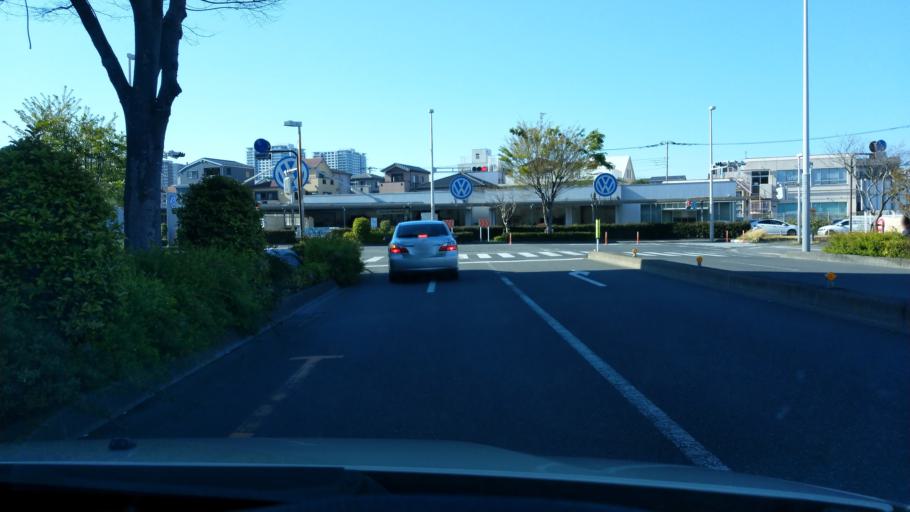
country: JP
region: Saitama
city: Yono
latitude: 35.8975
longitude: 139.6358
